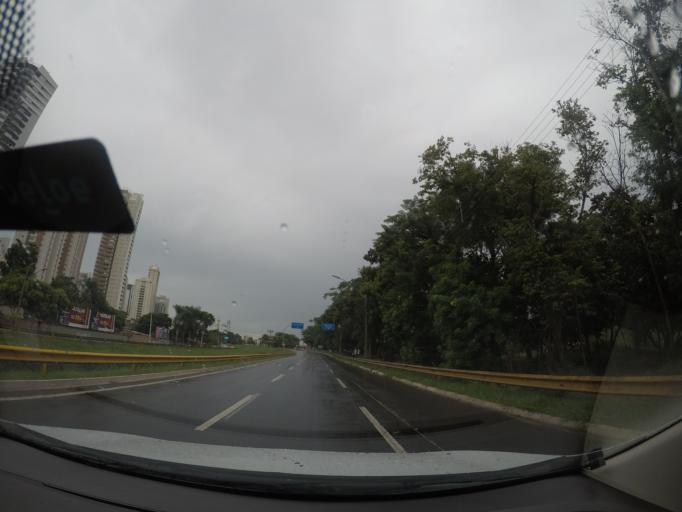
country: BR
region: Goias
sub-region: Goiania
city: Goiania
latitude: -16.6983
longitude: -49.2450
